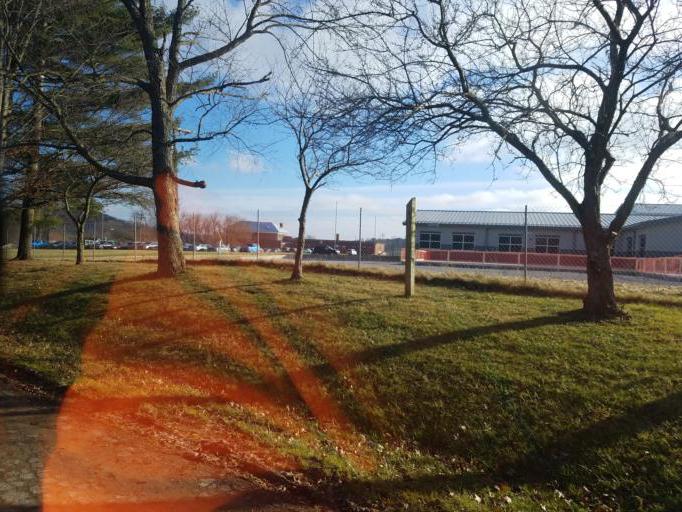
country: US
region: Ohio
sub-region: Sandusky County
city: Bellville
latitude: 40.5924
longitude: -82.4310
